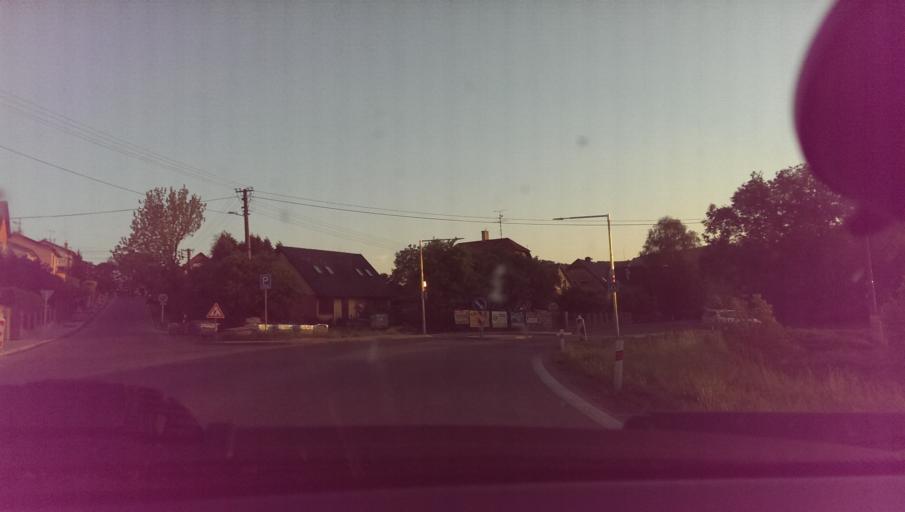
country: CZ
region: Zlin
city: Valasske Mezirici
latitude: 49.4600
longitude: 17.9742
